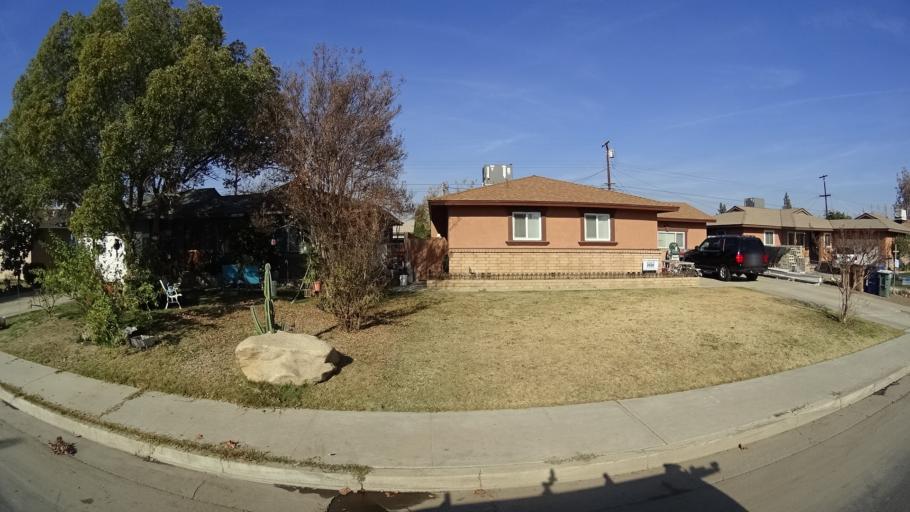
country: US
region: California
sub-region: Kern County
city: Bakersfield
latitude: 35.3266
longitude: -119.0190
